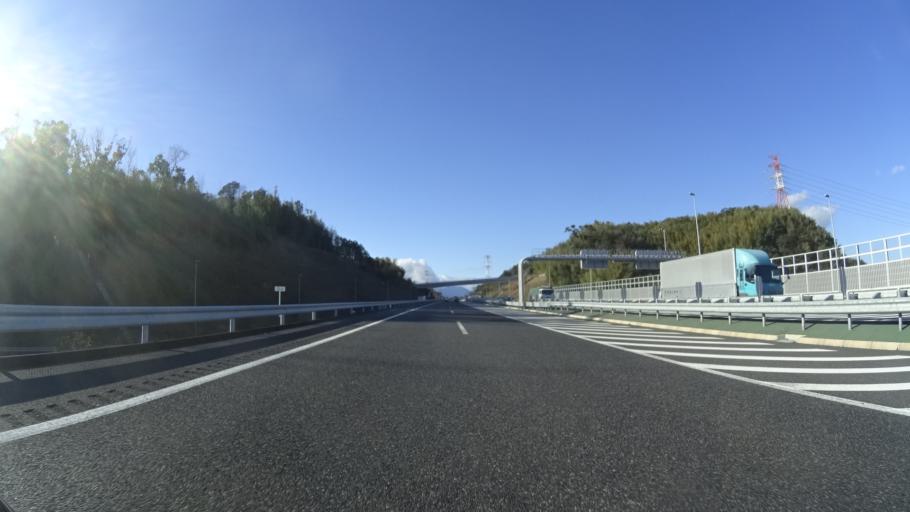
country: JP
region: Mie
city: Yokkaichi
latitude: 35.0392
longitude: 136.6258
